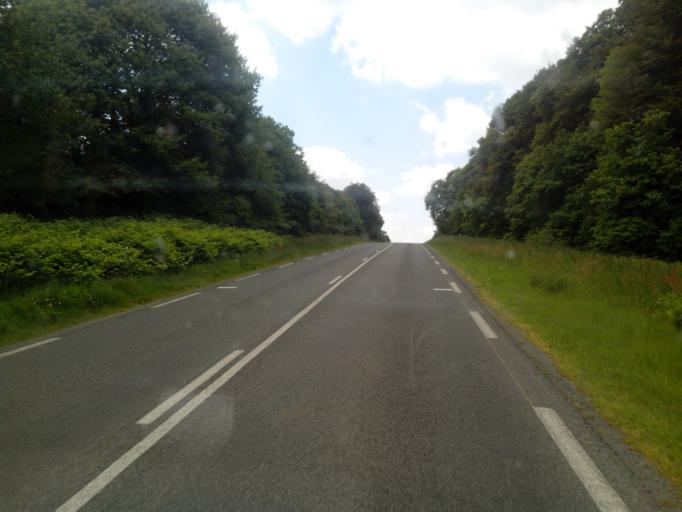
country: FR
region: Brittany
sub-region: Departement d'Ille-et-Vilaine
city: Landean
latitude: 48.3817
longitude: -1.1719
